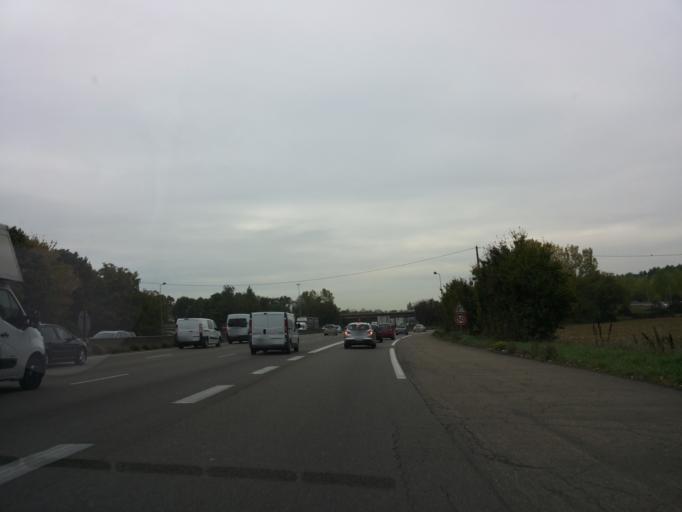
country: FR
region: Alsace
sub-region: Departement du Bas-Rhin
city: Ostwald
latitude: 48.5491
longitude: 7.7305
